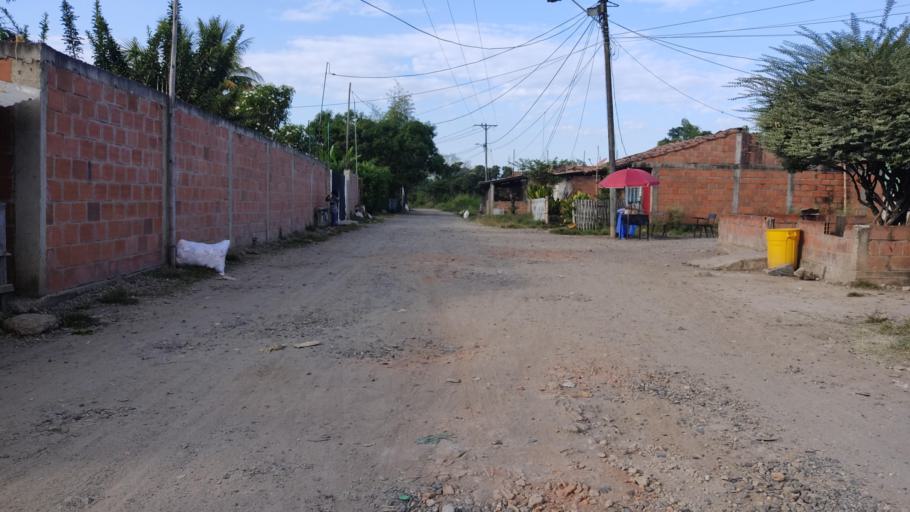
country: CO
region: Valle del Cauca
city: Jamundi
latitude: 3.1261
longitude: -76.5561
